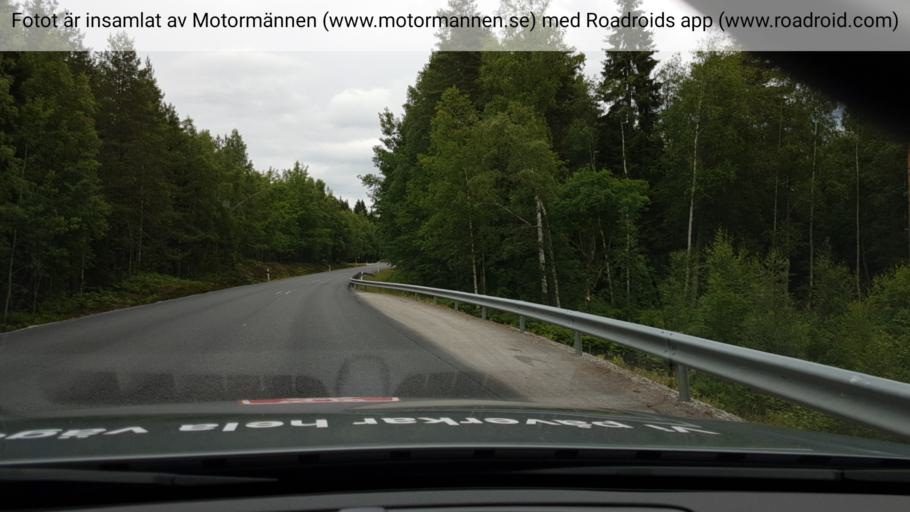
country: SE
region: Vaestmanland
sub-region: Skinnskattebergs Kommun
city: Skinnskatteberg
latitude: 59.8387
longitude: 15.5607
